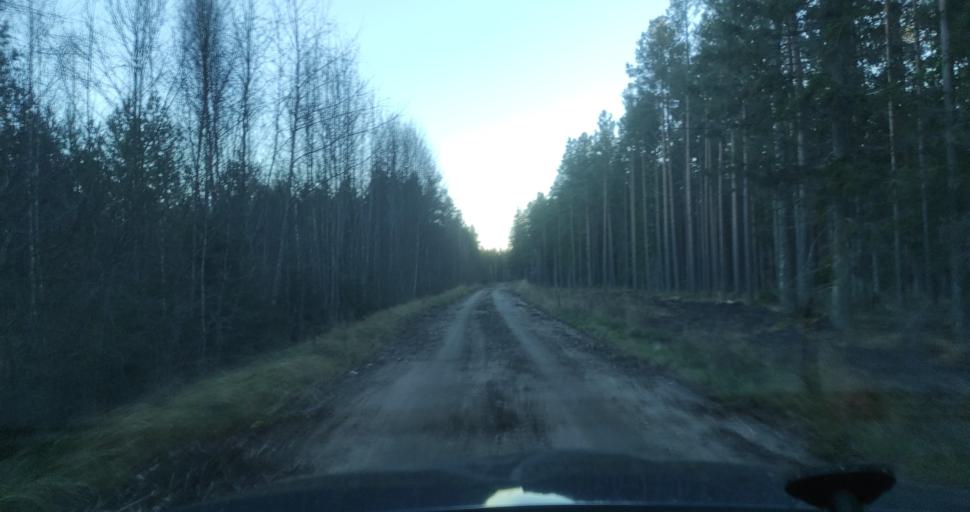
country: LV
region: Dundaga
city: Dundaga
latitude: 57.3821
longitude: 22.0811
